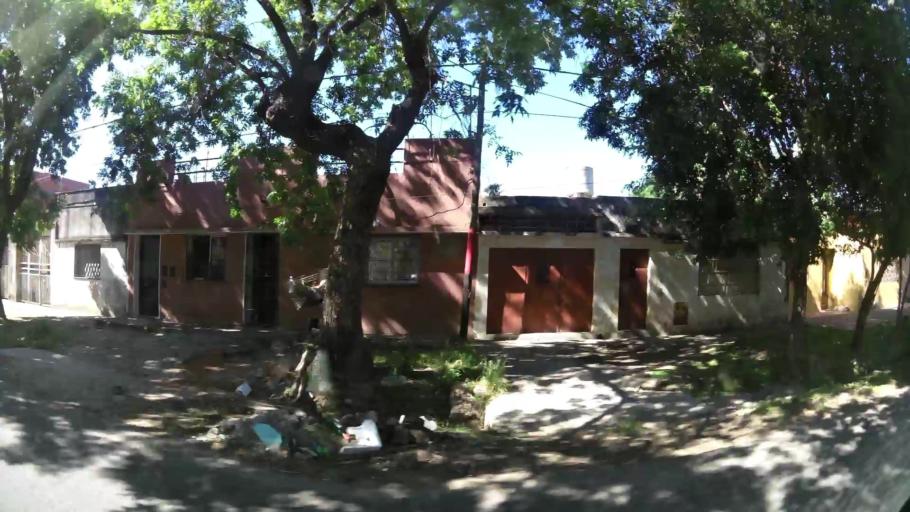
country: AR
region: Santa Fe
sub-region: Departamento de Rosario
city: Rosario
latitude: -32.9528
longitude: -60.6866
